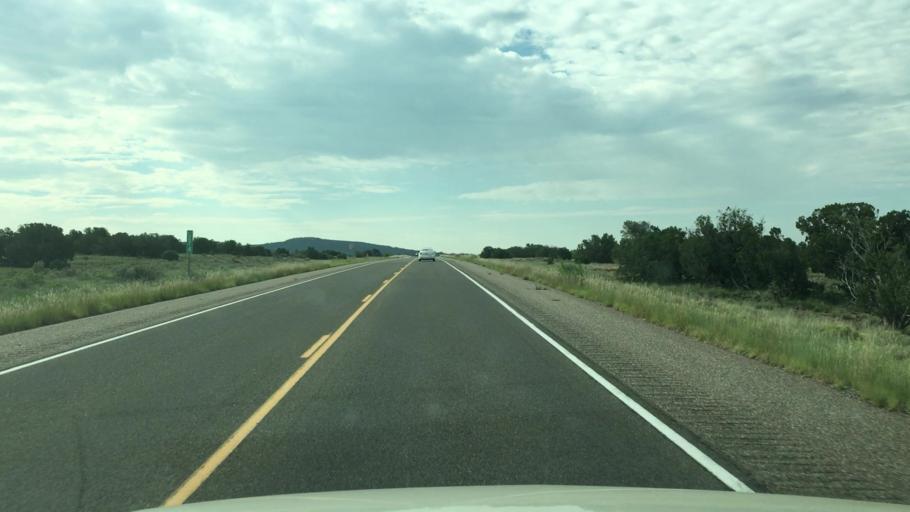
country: US
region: New Mexico
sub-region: Santa Fe County
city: Eldorado at Santa Fe
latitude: 35.3337
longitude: -105.8364
